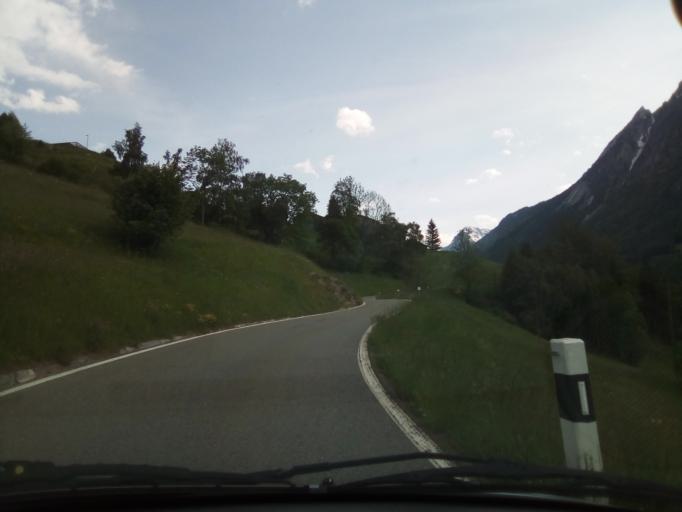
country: CH
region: Valais
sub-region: Entremont District
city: Orsieres
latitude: 46.0632
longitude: 7.1546
